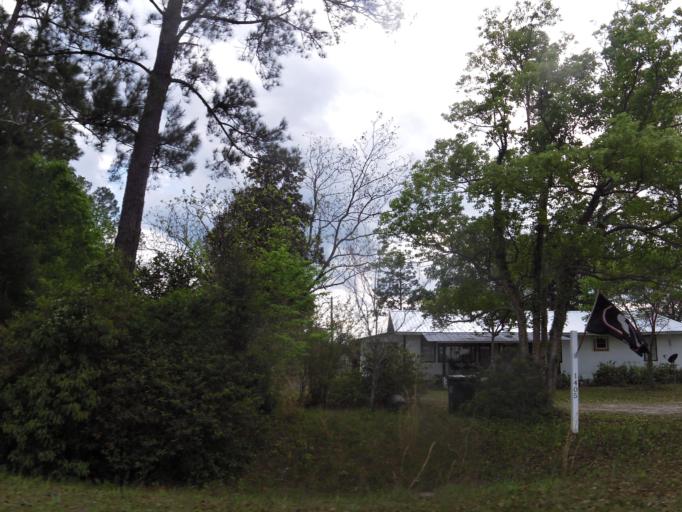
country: US
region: Georgia
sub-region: Charlton County
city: Folkston
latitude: 30.8079
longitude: -82.0520
